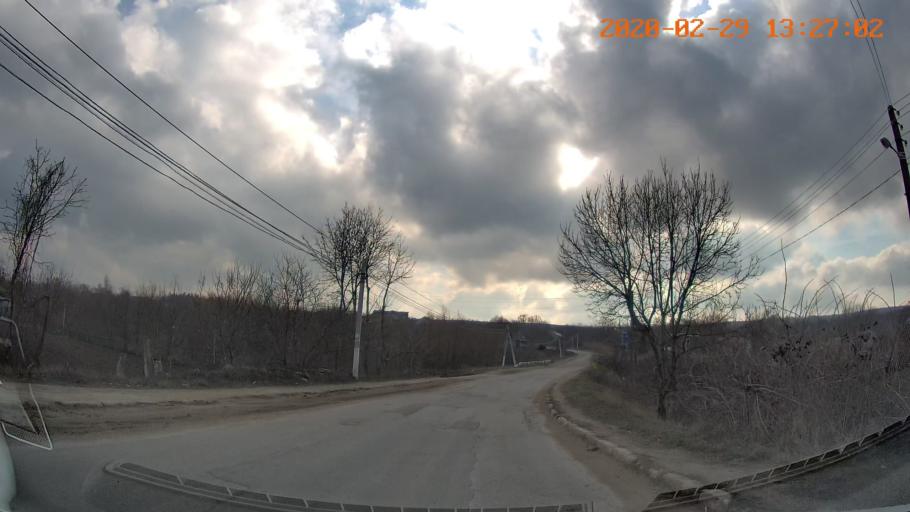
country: MD
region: Telenesti
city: Camenca
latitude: 47.9150
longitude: 28.6402
